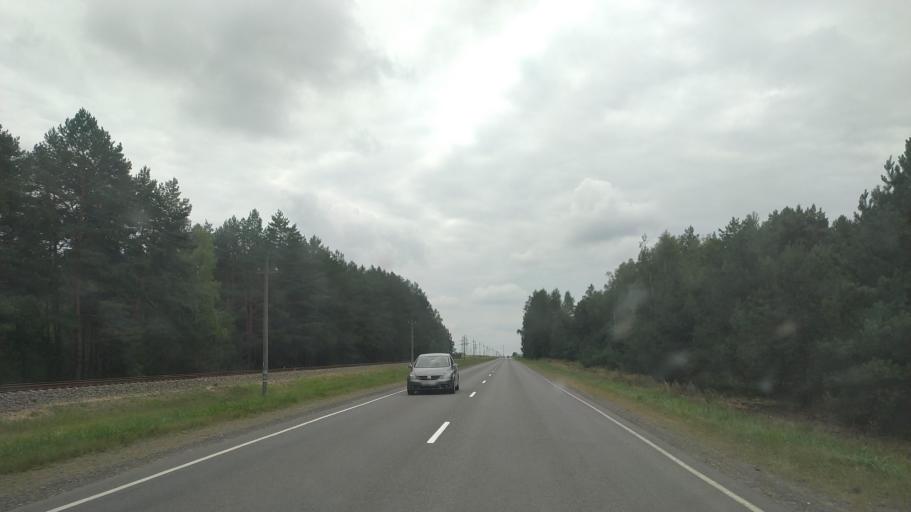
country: BY
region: Brest
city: Byelaazyorsk
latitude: 52.5256
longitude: 25.1474
